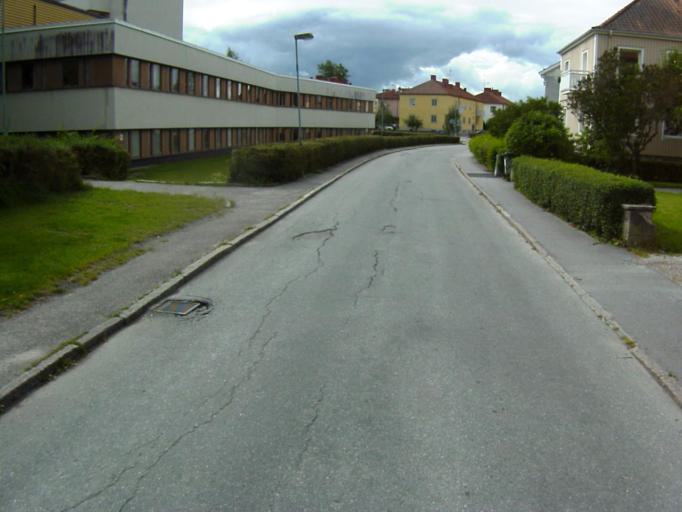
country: SE
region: Soedermanland
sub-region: Eskilstuna Kommun
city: Eskilstuna
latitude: 59.3651
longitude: 16.5306
